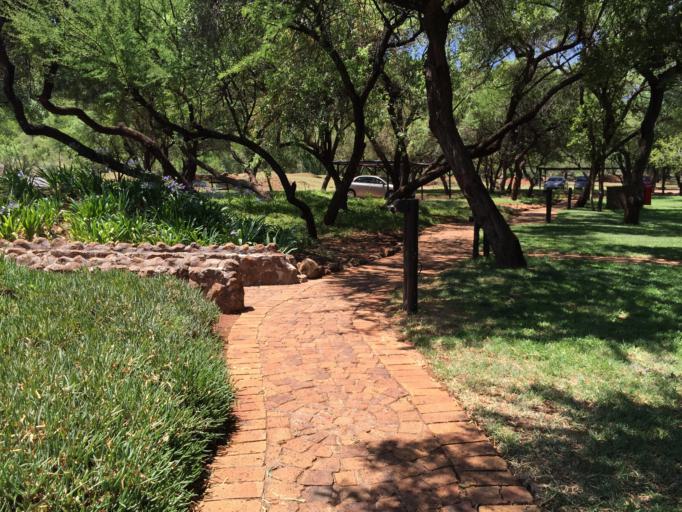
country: ZA
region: North-West
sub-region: Bojanala Platinum District Municipality
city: Mogwase
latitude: -25.3435
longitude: 27.0574
